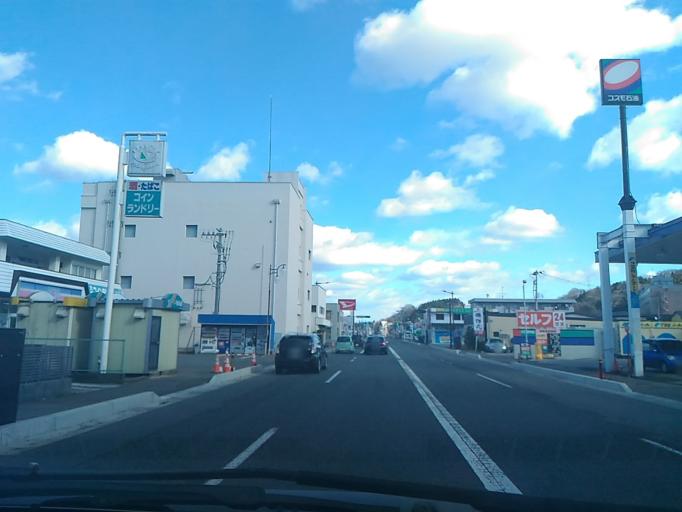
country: JP
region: Fukushima
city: Iwaki
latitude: 37.0377
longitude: 140.8604
